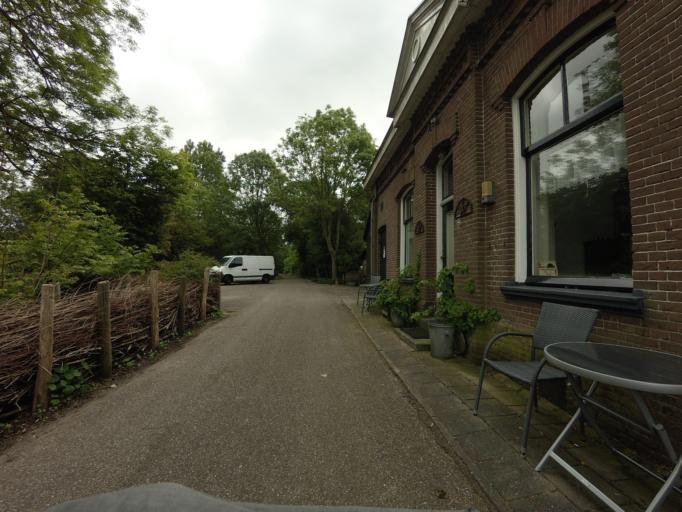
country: NL
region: North Holland
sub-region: Gemeente Beemster
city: Halfweg
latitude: 52.5400
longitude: 4.8389
